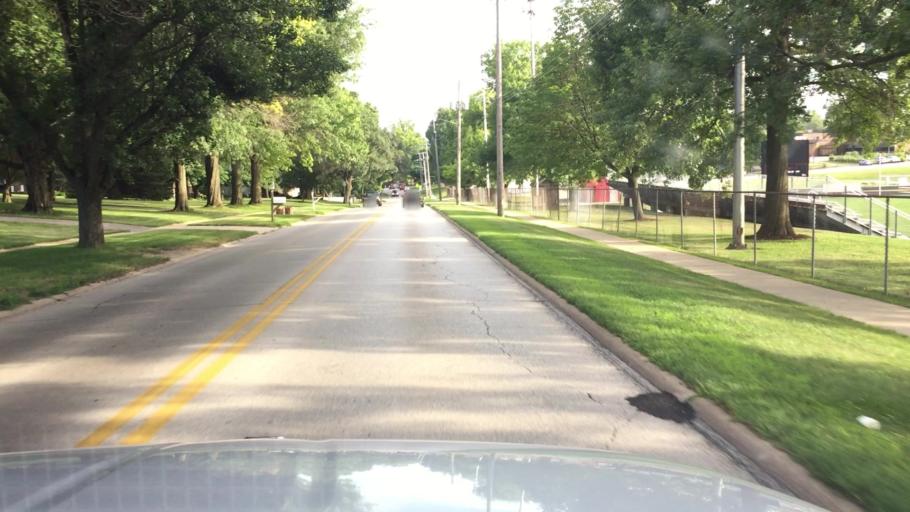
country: US
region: Iowa
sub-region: Johnson County
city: Iowa City
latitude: 41.6599
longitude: -91.5021
